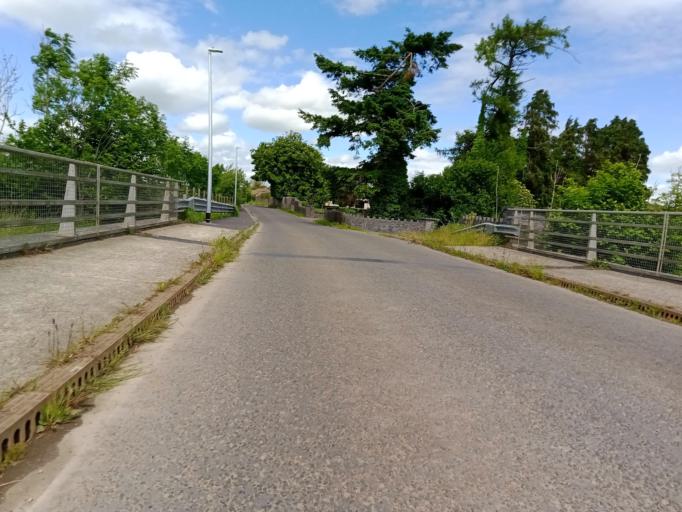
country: IE
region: Leinster
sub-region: Kilkenny
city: Kilkenny
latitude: 52.6770
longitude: -7.2490
